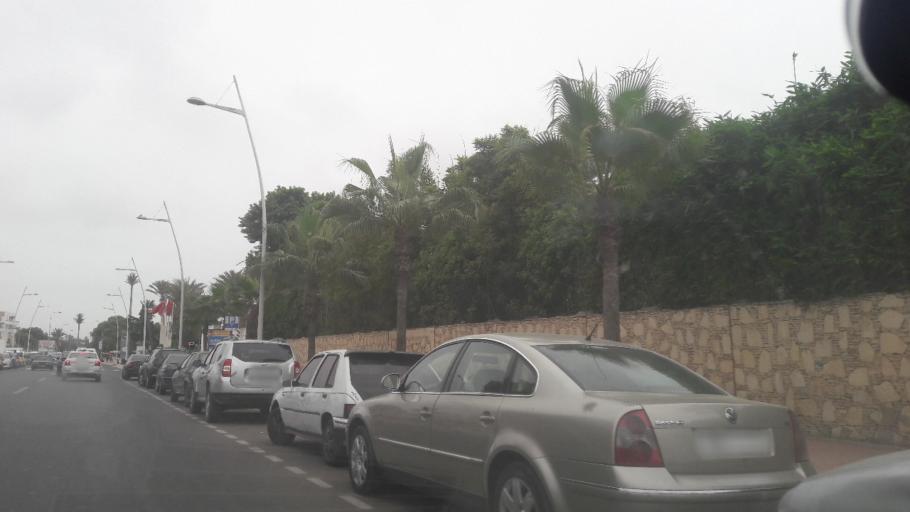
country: MA
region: Souss-Massa-Draa
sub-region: Agadir-Ida-ou-Tnan
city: Agadir
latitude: 30.4038
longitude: -9.5985
